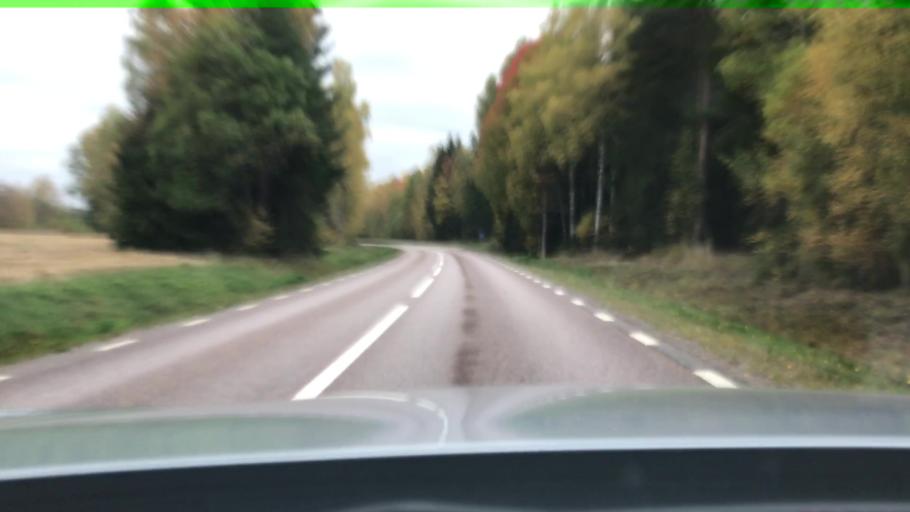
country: SE
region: Vaermland
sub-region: Eda Kommun
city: Amotfors
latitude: 59.7358
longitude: 12.2142
